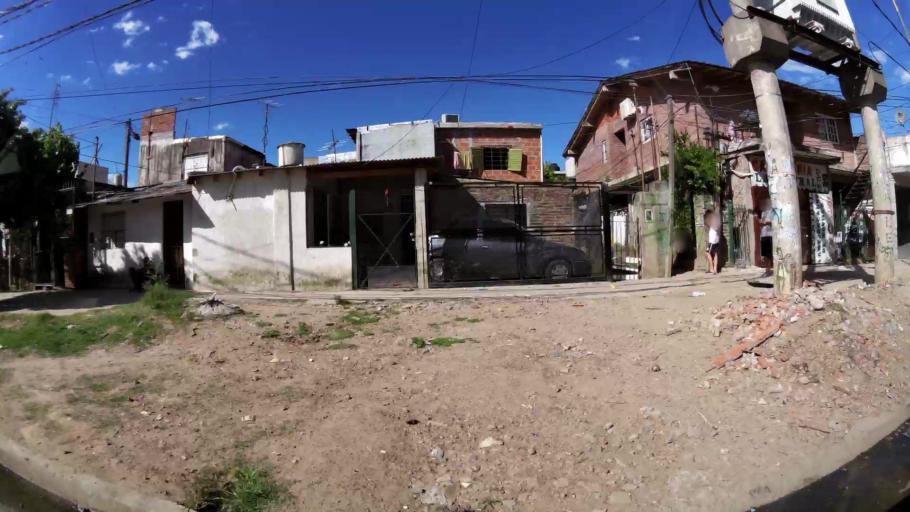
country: AR
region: Buenos Aires
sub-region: Partido de General San Martin
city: General San Martin
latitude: -34.5246
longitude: -58.5793
